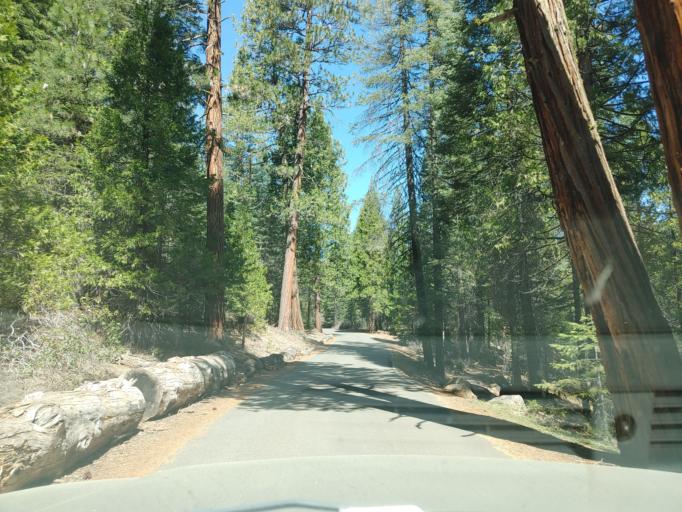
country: US
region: California
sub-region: Siskiyou County
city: McCloud
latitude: 41.2413
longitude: -122.0255
